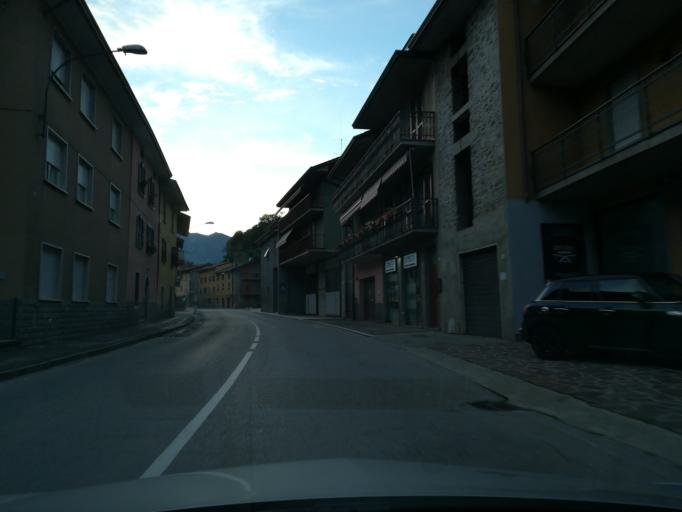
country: IT
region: Lombardy
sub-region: Provincia di Bergamo
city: Bedulita
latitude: 45.7972
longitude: 9.5588
